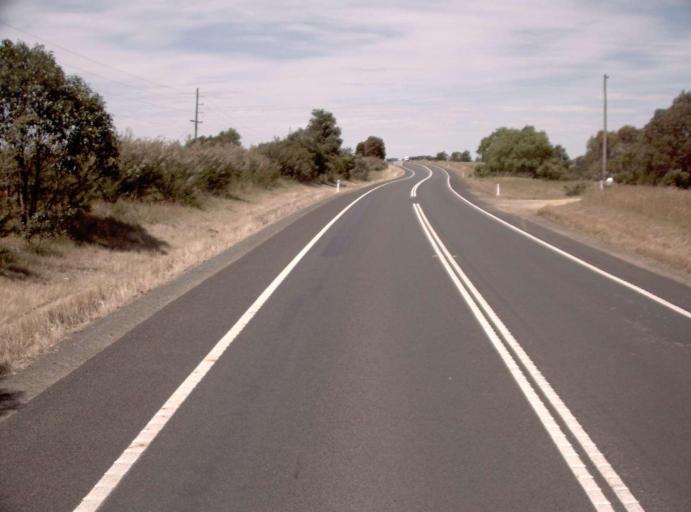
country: AU
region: Victoria
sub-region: Wellington
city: Heyfield
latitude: -38.1292
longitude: 146.8290
